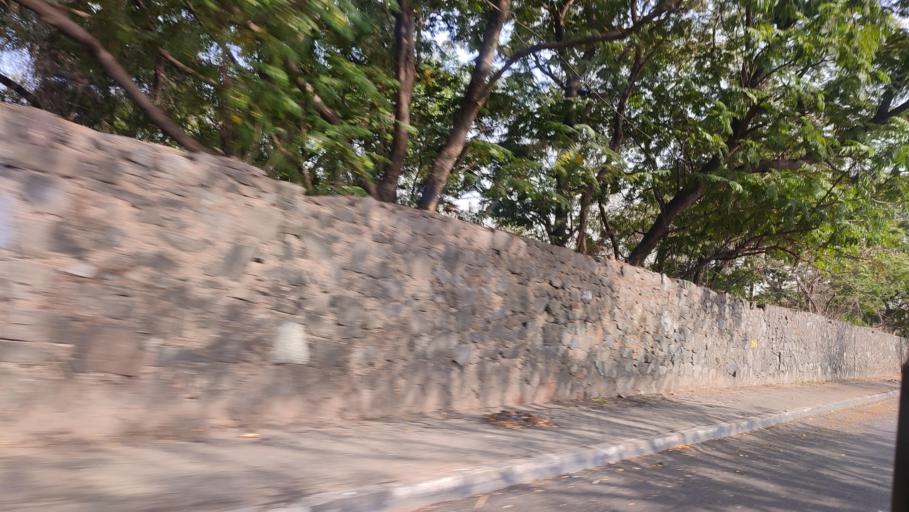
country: IN
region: Maharashtra
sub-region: Mumbai Suburban
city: Powai
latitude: 19.0998
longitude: 72.9289
